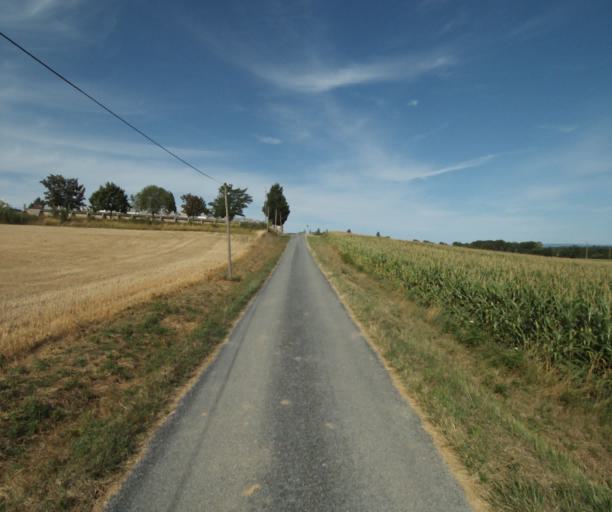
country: FR
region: Midi-Pyrenees
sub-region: Departement du Tarn
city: Puylaurens
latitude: 43.5232
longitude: 2.0555
